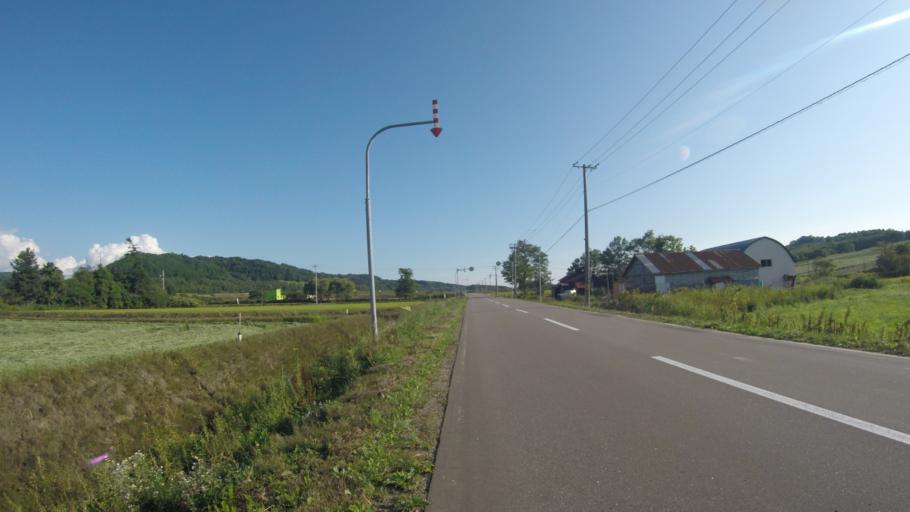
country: JP
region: Hokkaido
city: Iwamizawa
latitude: 43.1940
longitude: 141.8243
